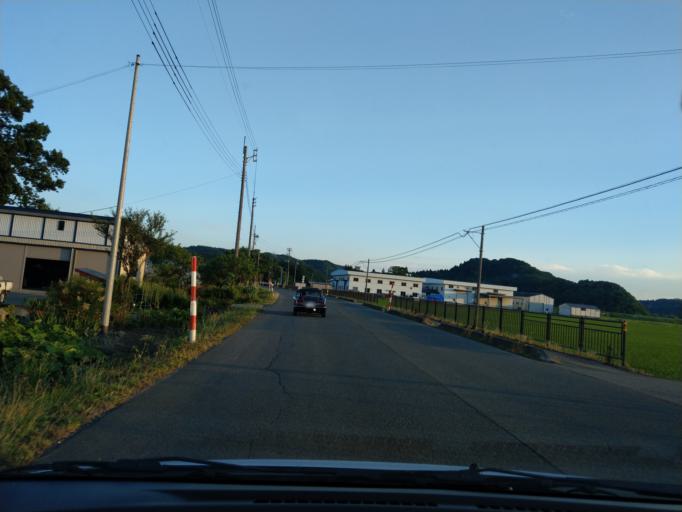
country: JP
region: Akita
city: Kakunodatemachi
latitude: 39.6173
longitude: 140.5715
